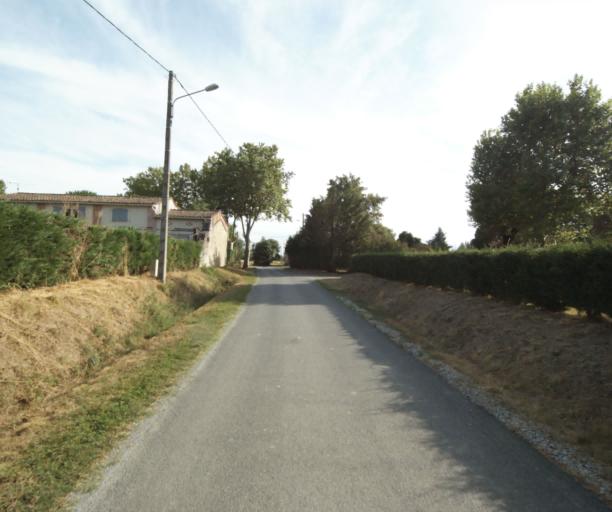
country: FR
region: Midi-Pyrenees
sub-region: Departement de la Haute-Garonne
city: Revel
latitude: 43.5026
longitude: 1.9962
